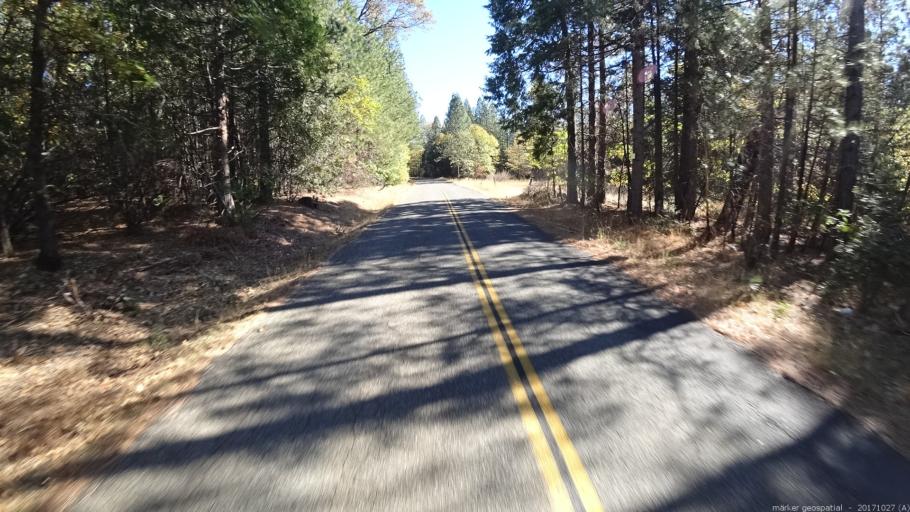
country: US
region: California
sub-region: Shasta County
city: Bella Vista
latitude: 40.7189
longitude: -122.0035
